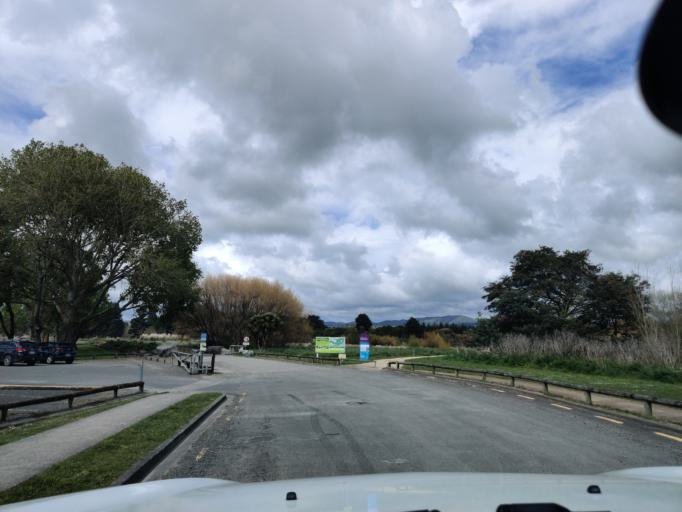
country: NZ
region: Manawatu-Wanganui
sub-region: Palmerston North City
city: Palmerston North
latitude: -40.3827
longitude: 175.5873
